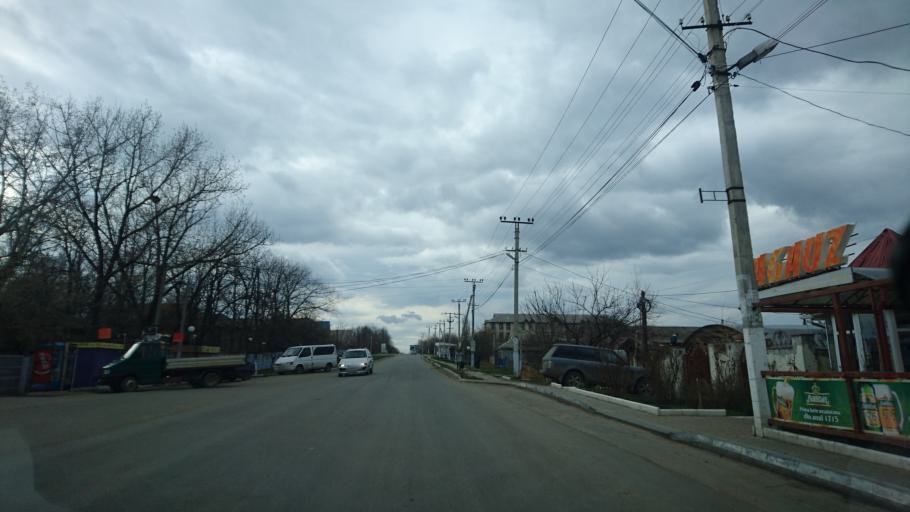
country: MD
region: Gagauzia
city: Comrat
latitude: 46.3034
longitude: 28.6382
